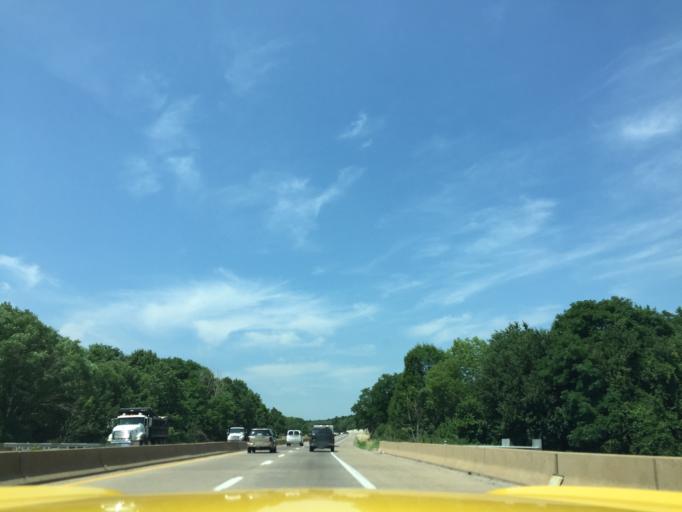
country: US
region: Pennsylvania
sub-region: Bucks County
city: Fairless Hills
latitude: 40.1943
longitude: -74.8235
